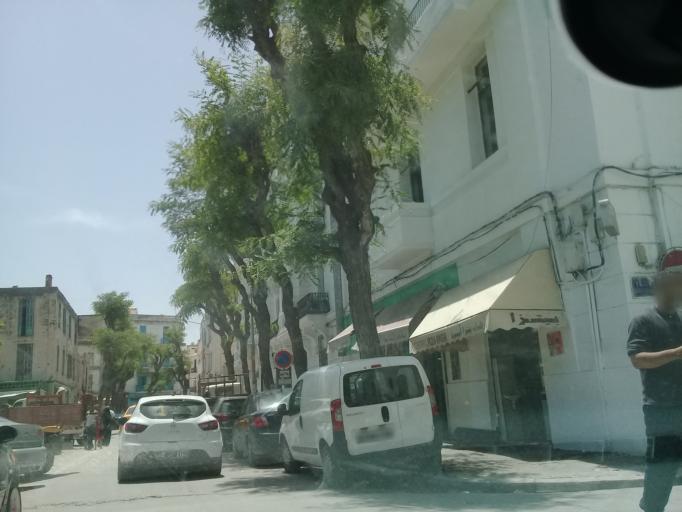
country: TN
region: Tunis
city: Tunis
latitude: 36.7955
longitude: 10.1791
